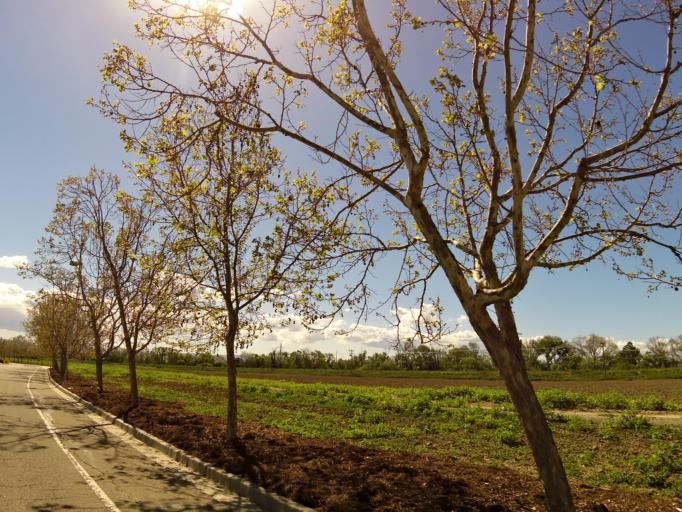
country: US
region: California
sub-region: Santa Clara County
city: Milpitas
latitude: 37.4409
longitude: -121.9225
